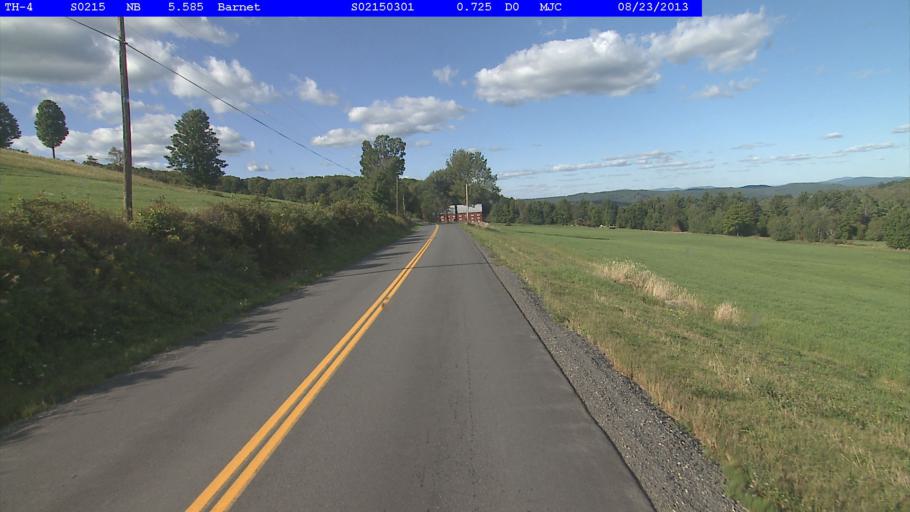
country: US
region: New Hampshire
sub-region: Grafton County
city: Woodsville
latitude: 44.2845
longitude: -72.1708
